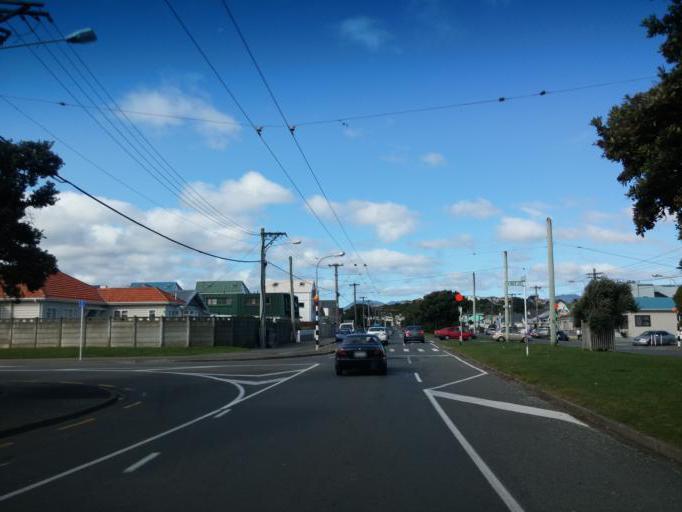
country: NZ
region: Wellington
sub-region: Wellington City
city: Wellington
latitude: -41.3181
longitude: 174.7968
